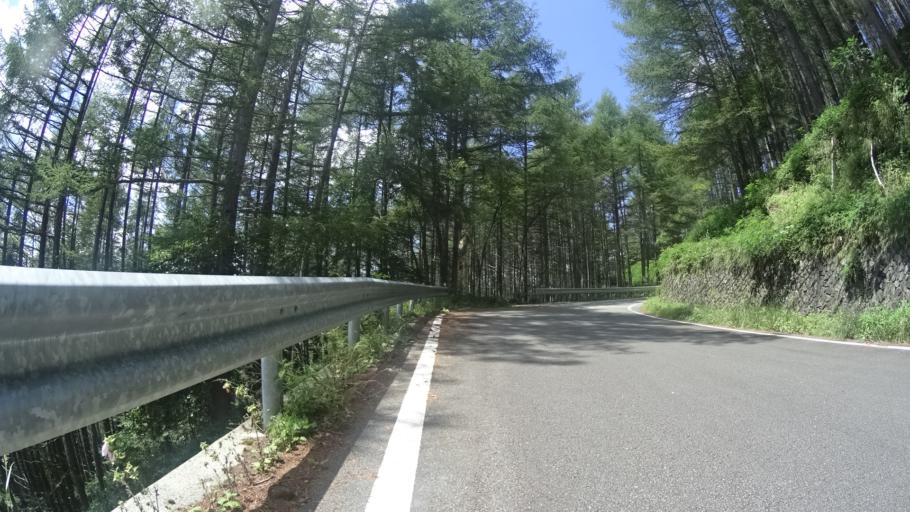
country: JP
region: Yamanashi
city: Enzan
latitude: 35.8412
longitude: 138.6425
